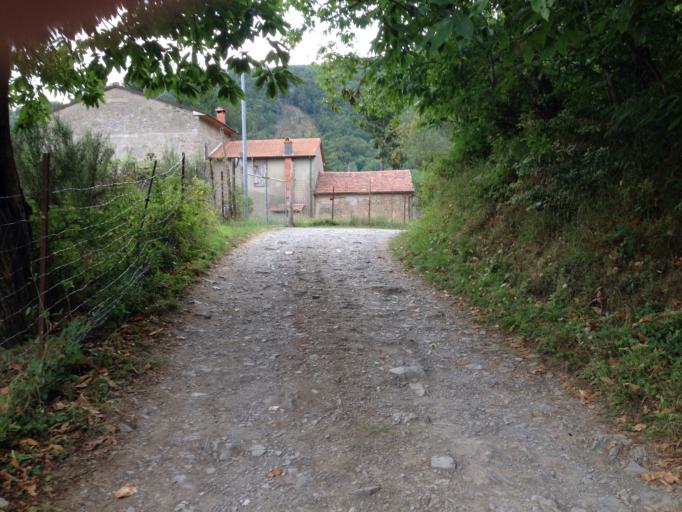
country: IT
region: Tuscany
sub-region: Provincia di Prato
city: Cantagallo
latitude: 44.0722
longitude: 11.0917
